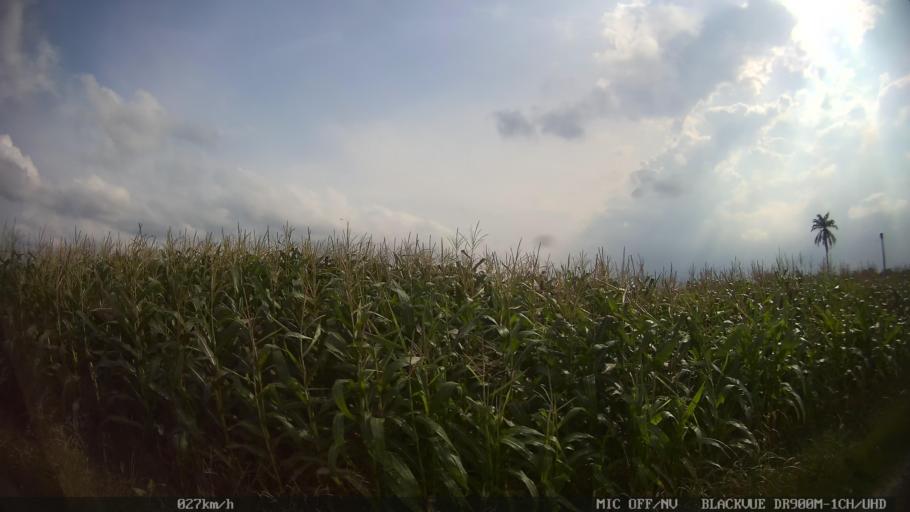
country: ID
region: North Sumatra
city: Percut
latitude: 3.5700
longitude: 98.7776
